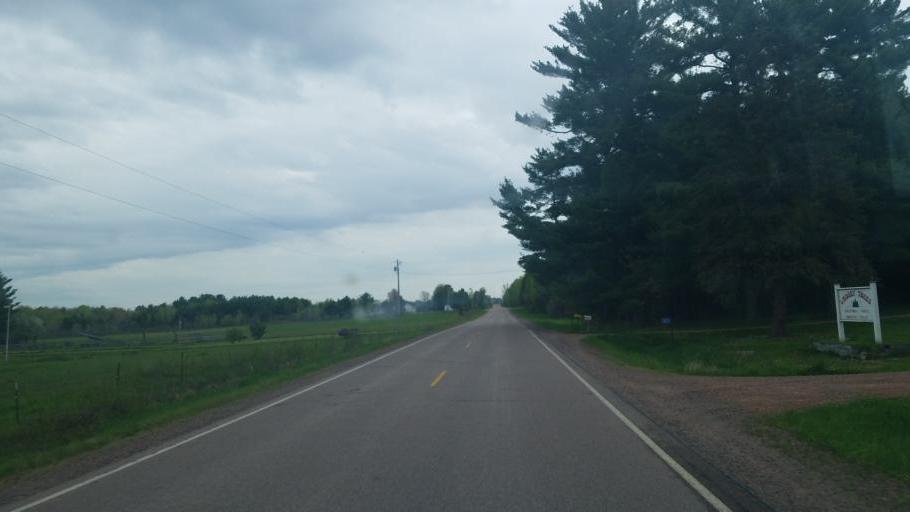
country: US
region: Wisconsin
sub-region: Wood County
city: Marshfield
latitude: 44.5674
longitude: -90.2998
